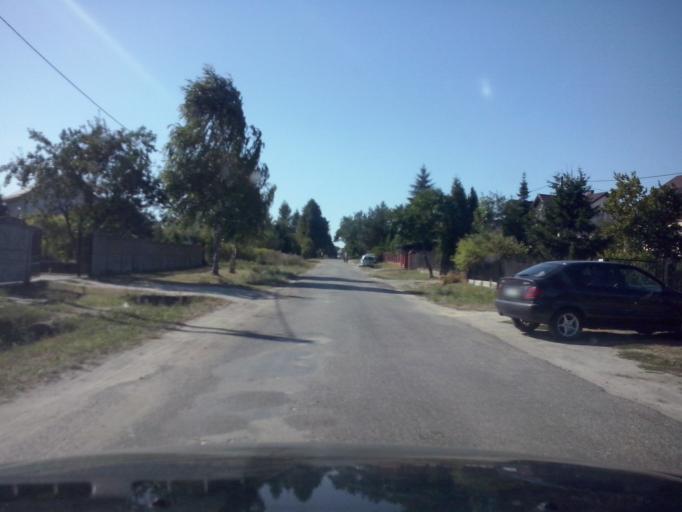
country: PL
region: Swietokrzyskie
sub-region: Powiat kielecki
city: Chmielnik
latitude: 50.6119
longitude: 20.7258
